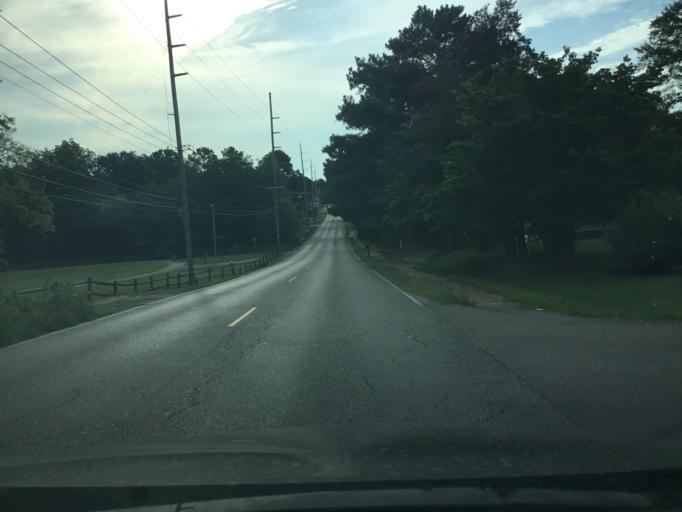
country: US
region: Alabama
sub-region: Montgomery County
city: Montgomery
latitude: 32.3671
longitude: -86.2490
